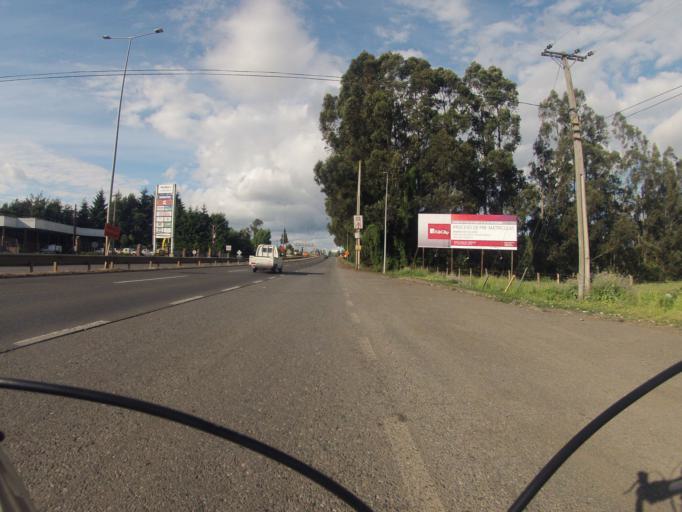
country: CL
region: Araucania
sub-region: Provincia de Cautin
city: Temuco
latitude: -38.7802
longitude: -72.6103
